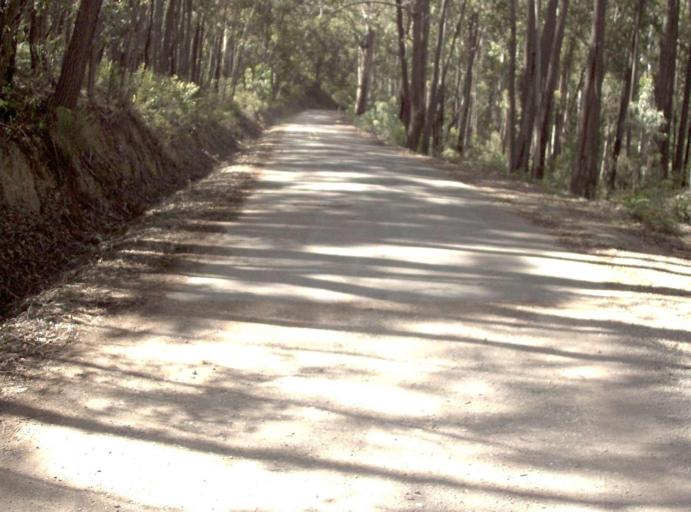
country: AU
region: Victoria
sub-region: East Gippsland
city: Lakes Entrance
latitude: -37.3920
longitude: 148.1228
